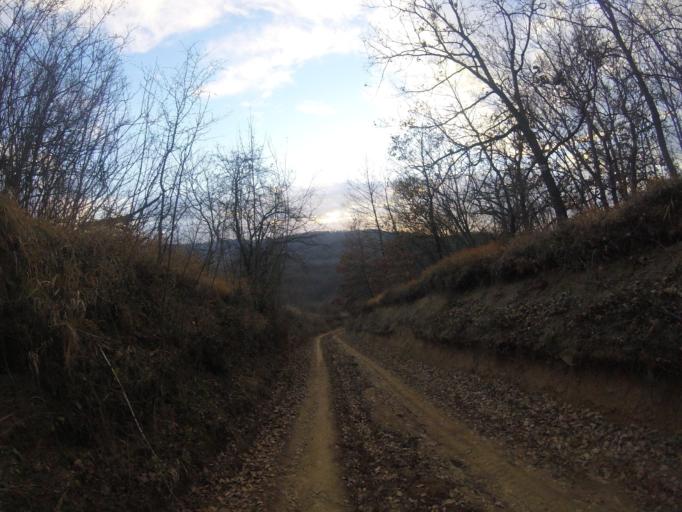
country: HU
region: Tolna
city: Bonyhad
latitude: 46.2229
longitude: 18.6109
